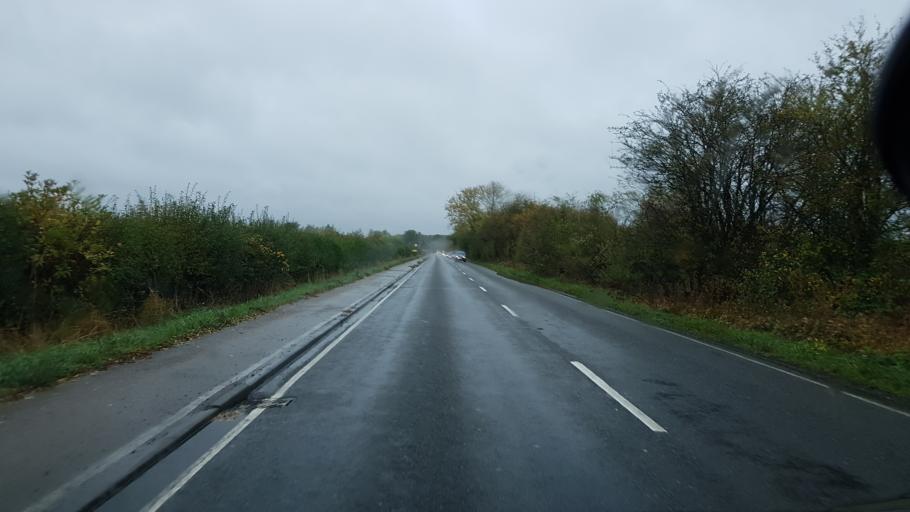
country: GB
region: England
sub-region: Oxfordshire
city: Marcham
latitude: 51.6684
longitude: -1.3304
